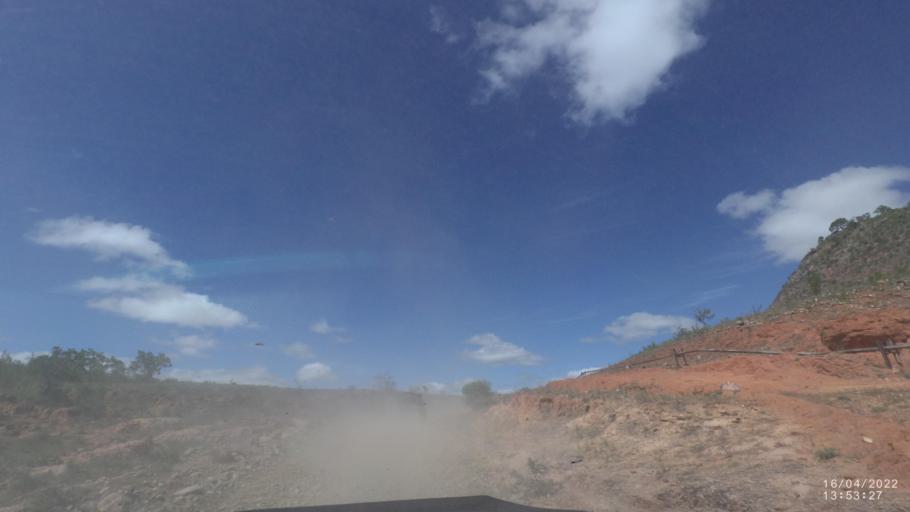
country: BO
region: Cochabamba
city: Mizque
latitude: -18.0244
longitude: -65.5712
